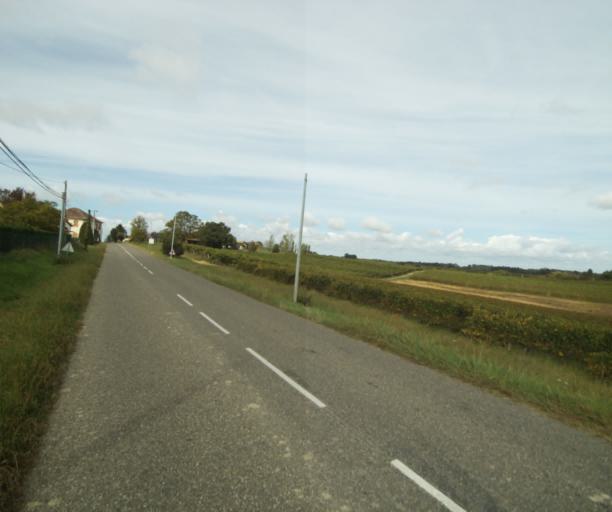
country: FR
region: Midi-Pyrenees
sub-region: Departement du Gers
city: Eauze
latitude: 43.8447
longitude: 0.1443
